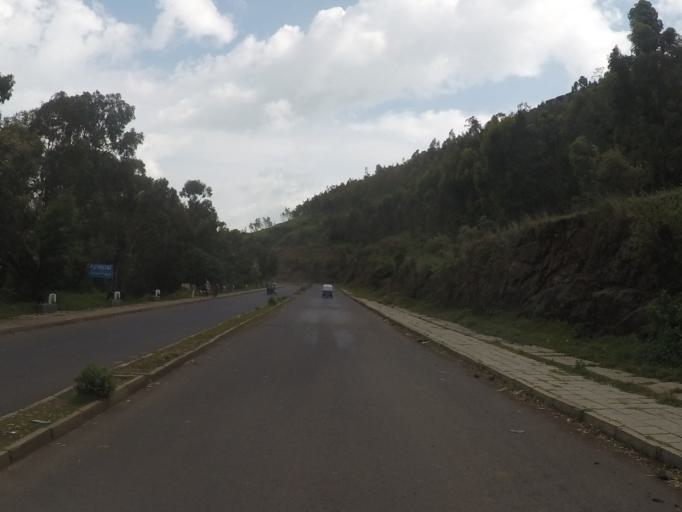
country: ET
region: Amhara
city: Gondar
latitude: 12.6318
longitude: 37.4695
